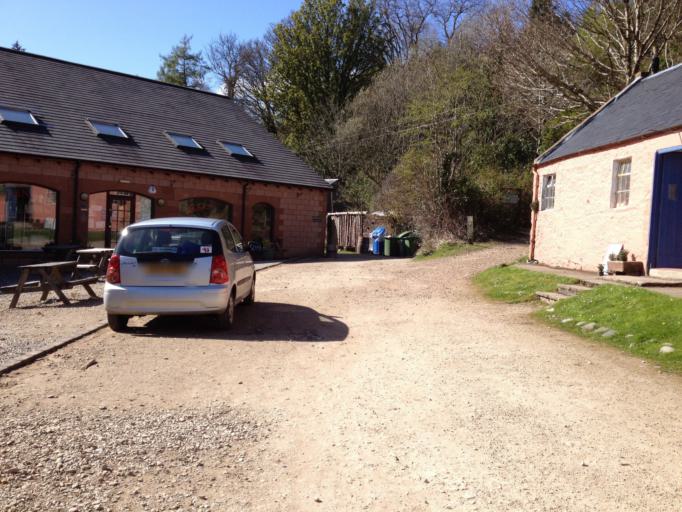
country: GB
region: Scotland
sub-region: North Ayrshire
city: Isle of Arran
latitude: 55.5922
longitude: -5.1564
